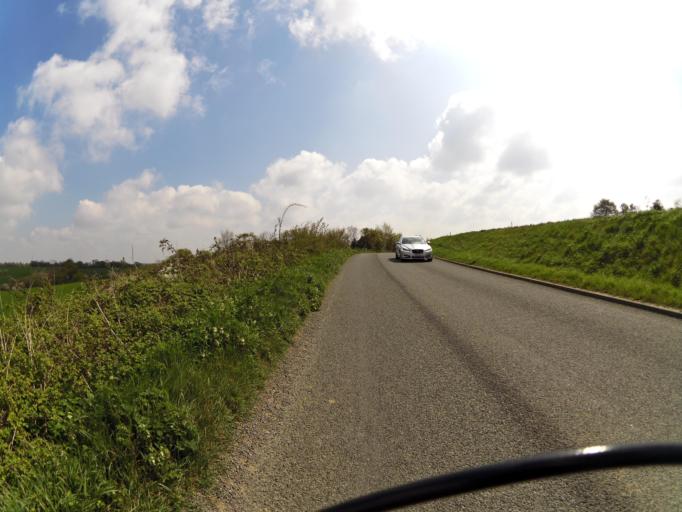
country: GB
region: England
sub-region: Suffolk
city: Hadleigh
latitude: 52.0744
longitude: 0.9544
